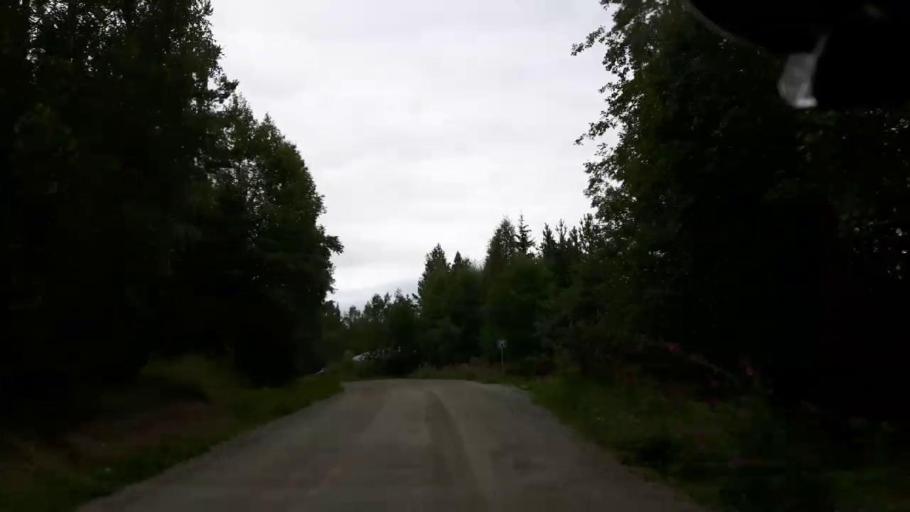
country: SE
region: Jaemtland
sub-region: Braecke Kommun
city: Braecke
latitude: 62.8311
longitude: 15.6900
